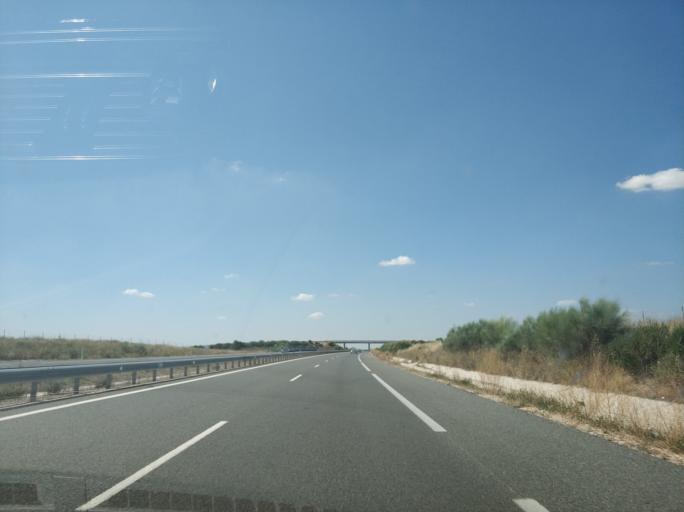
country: ES
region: Castille and Leon
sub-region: Provincia de Salamanca
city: Castellanos de Villiquera
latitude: 41.0580
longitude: -5.6792
